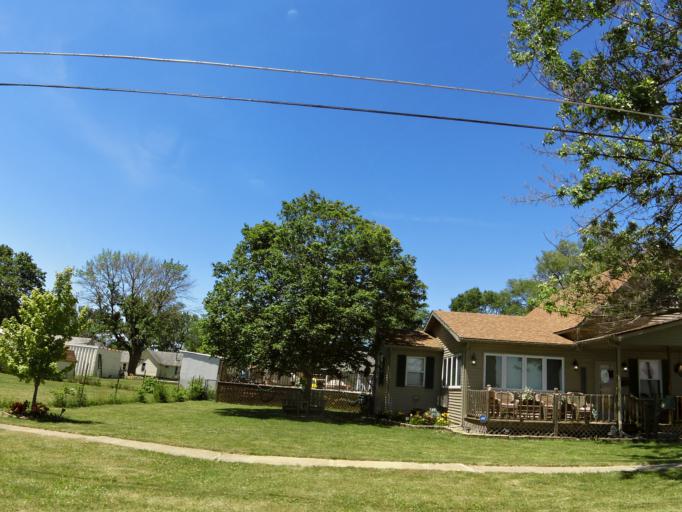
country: US
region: Illinois
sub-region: Iroquois County
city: Milford
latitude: 40.6312
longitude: -87.6911
